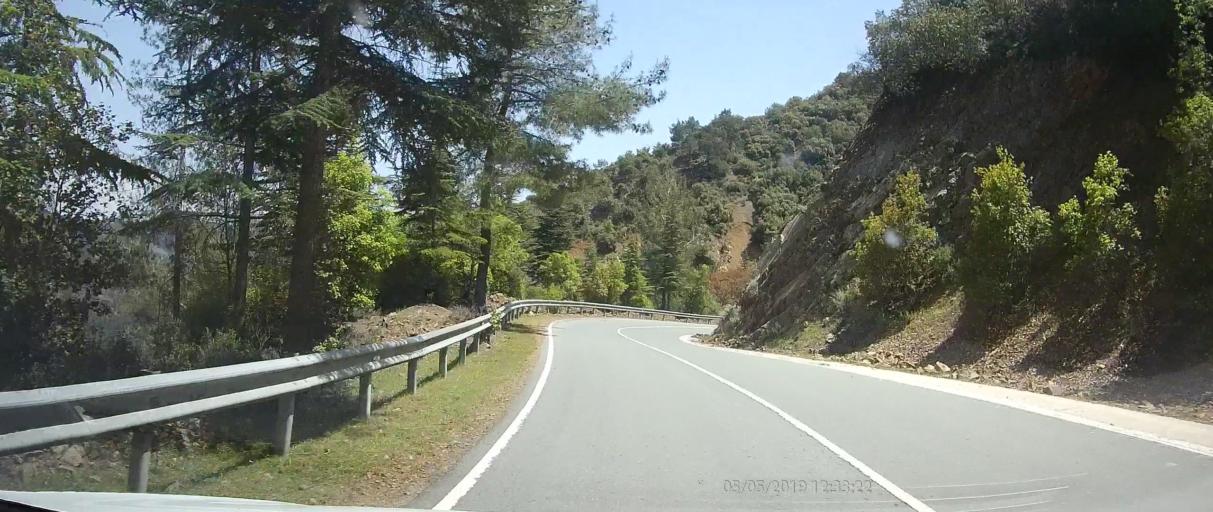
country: CY
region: Lefkosia
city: Kakopetria
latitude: 34.9795
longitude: 32.7621
